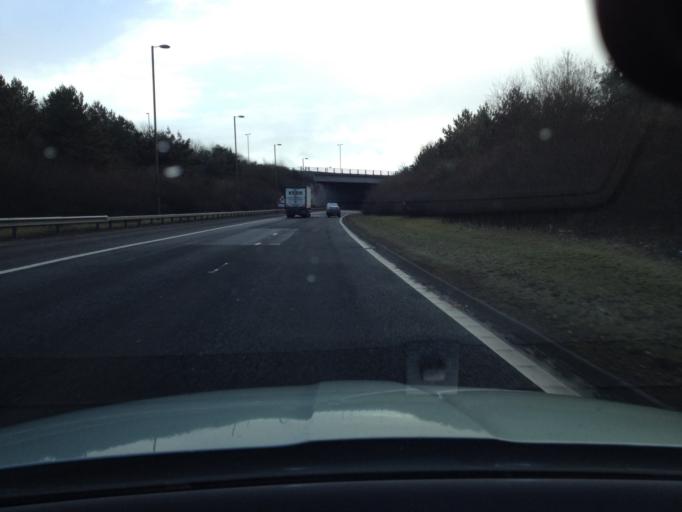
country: GB
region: Scotland
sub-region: Edinburgh
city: Newbridge
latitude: 55.9276
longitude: -3.4044
